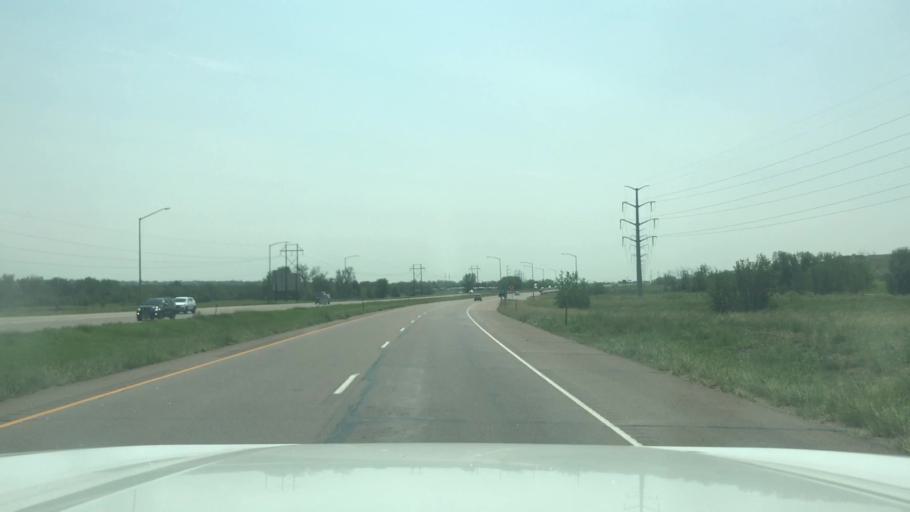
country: US
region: Colorado
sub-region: El Paso County
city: Security-Widefield
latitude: 38.7227
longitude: -104.7309
